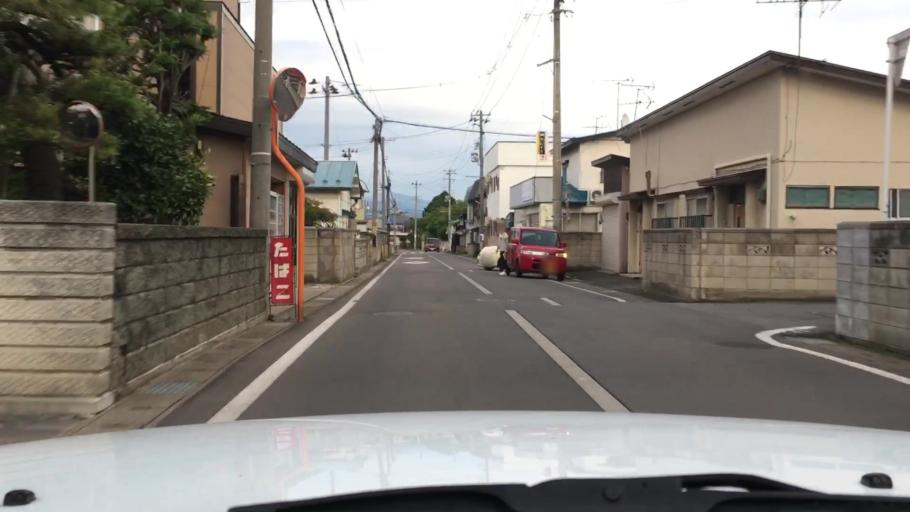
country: JP
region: Aomori
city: Hirosaki
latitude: 40.5935
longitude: 140.4898
